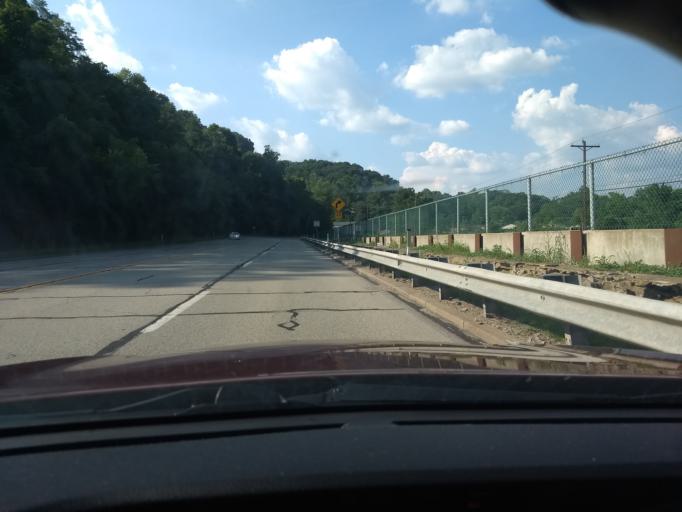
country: US
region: Pennsylvania
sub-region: Allegheny County
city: White Oak
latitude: 40.3259
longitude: -79.8181
